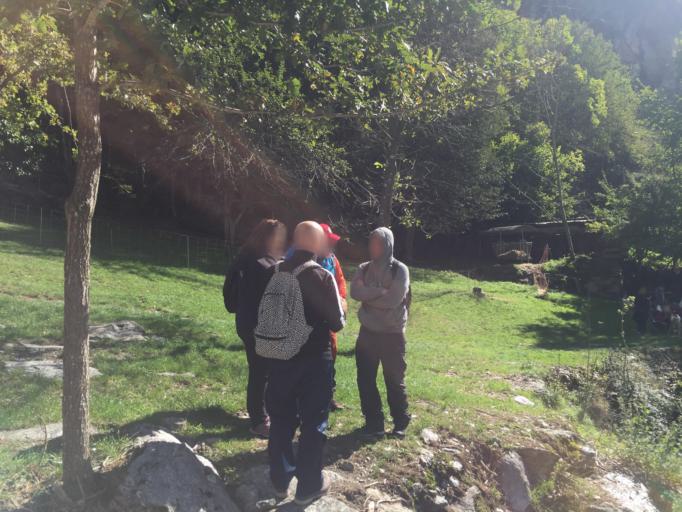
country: IT
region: Piedmont
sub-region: Provincia Verbano-Cusio-Ossola
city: Baceno
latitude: 46.2532
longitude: 8.3321
